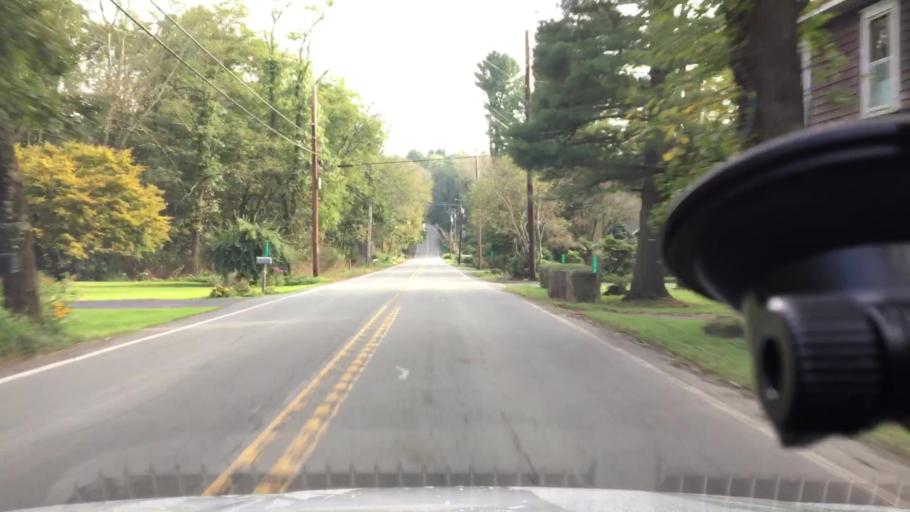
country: US
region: Pennsylvania
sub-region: Monroe County
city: Parkside
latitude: 41.1232
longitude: -75.2817
